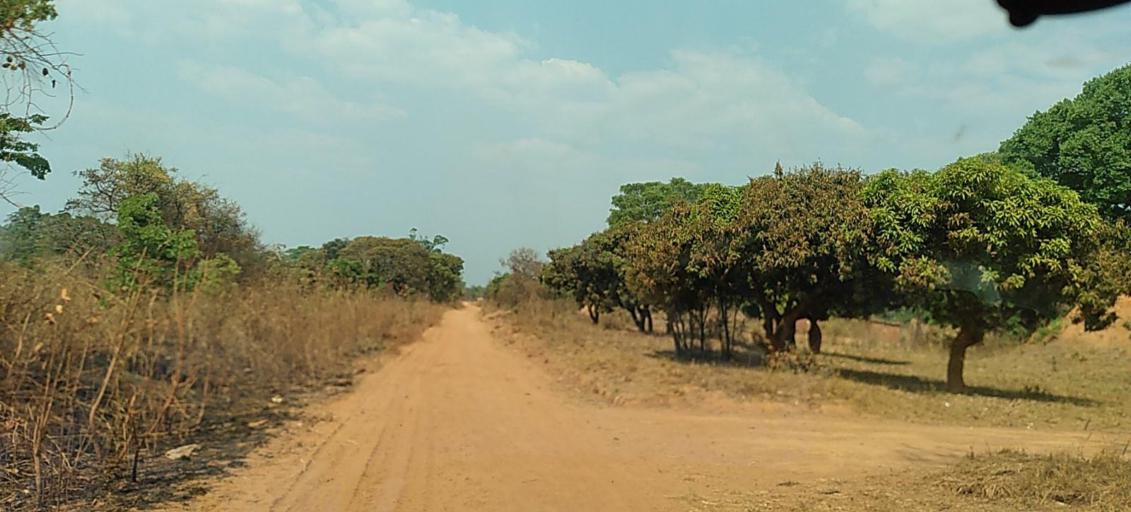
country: ZM
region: North-Western
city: Kasempa
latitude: -13.3057
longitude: 26.0738
